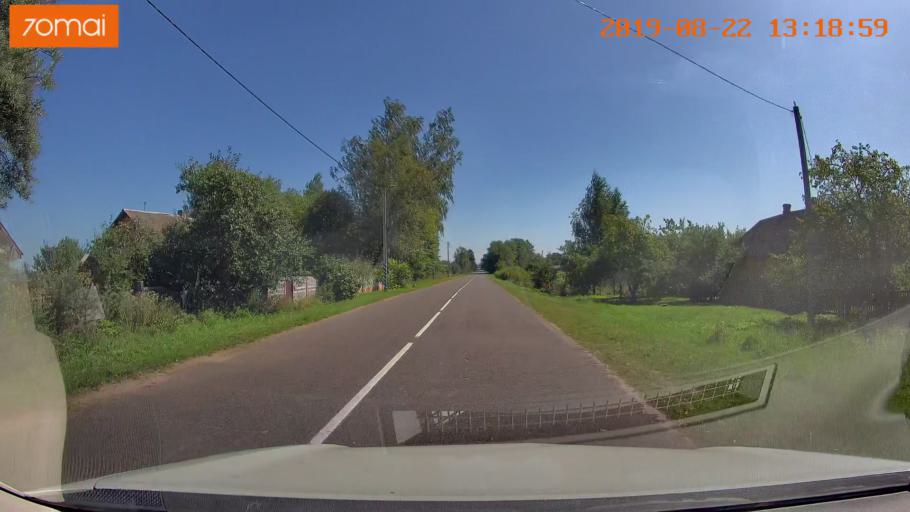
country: BY
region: Minsk
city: Urechcha
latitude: 53.2372
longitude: 27.9452
